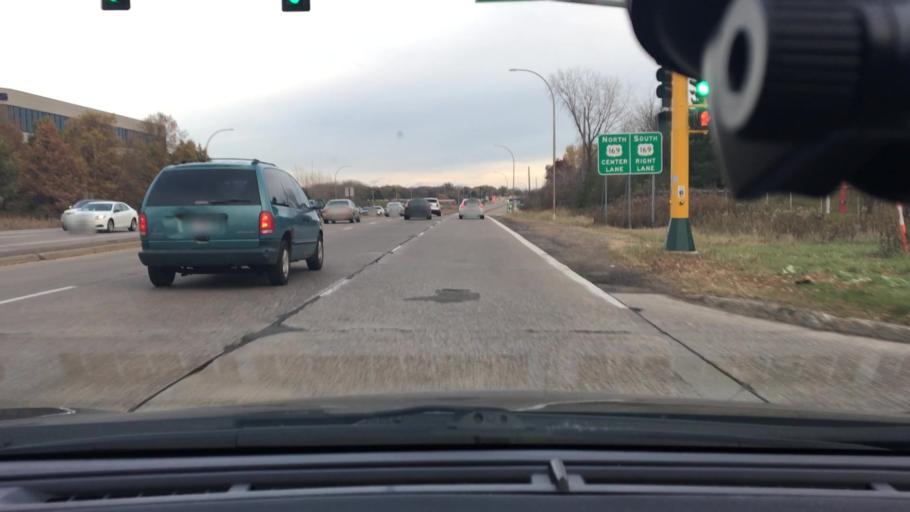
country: US
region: Minnesota
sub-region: Hennepin County
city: New Hope
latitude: 45.0583
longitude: -93.4080
